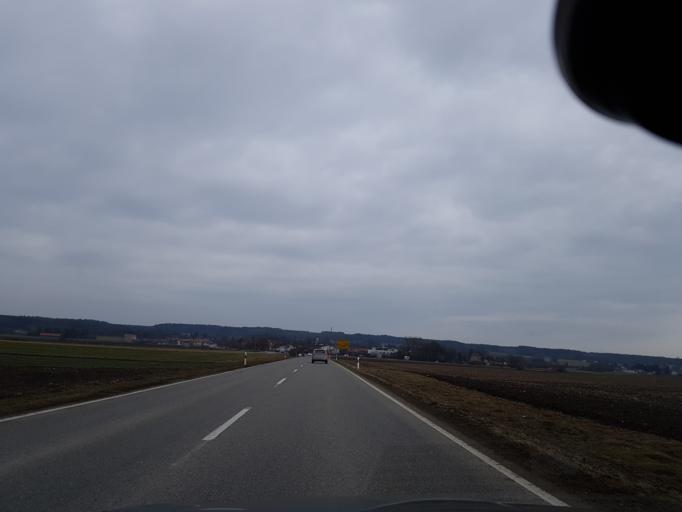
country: DE
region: Bavaria
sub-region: Upper Bavaria
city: Aying
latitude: 47.9721
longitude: 11.7602
